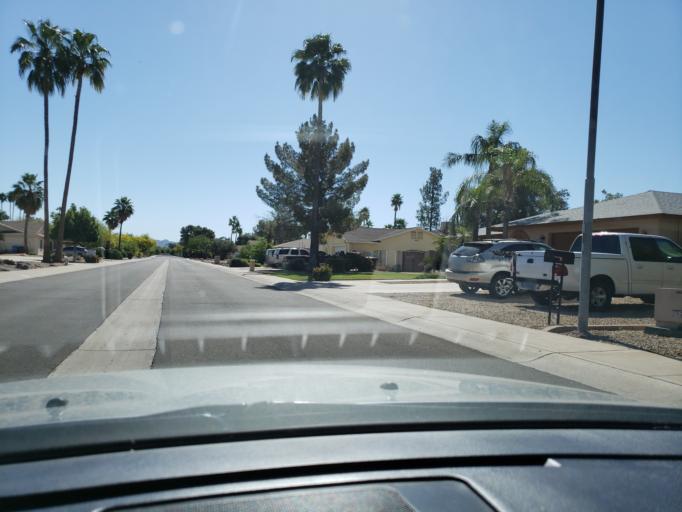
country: US
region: Arizona
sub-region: Maricopa County
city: Paradise Valley
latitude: 33.6124
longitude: -111.9538
